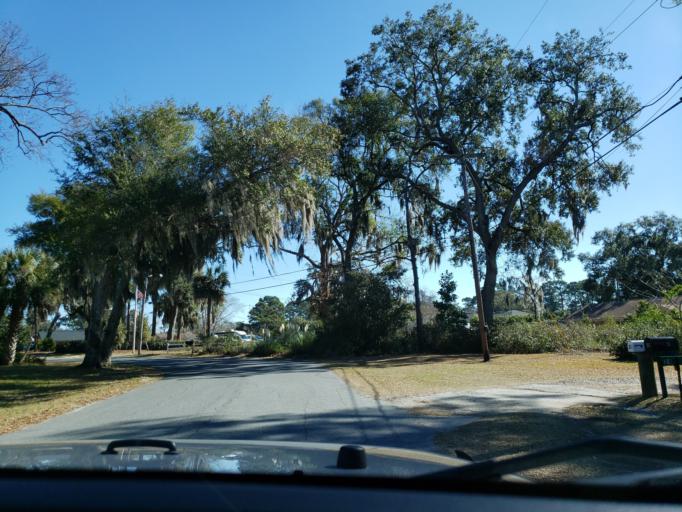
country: US
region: Georgia
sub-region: Chatham County
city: Wilmington Island
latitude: 32.0356
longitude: -80.9691
